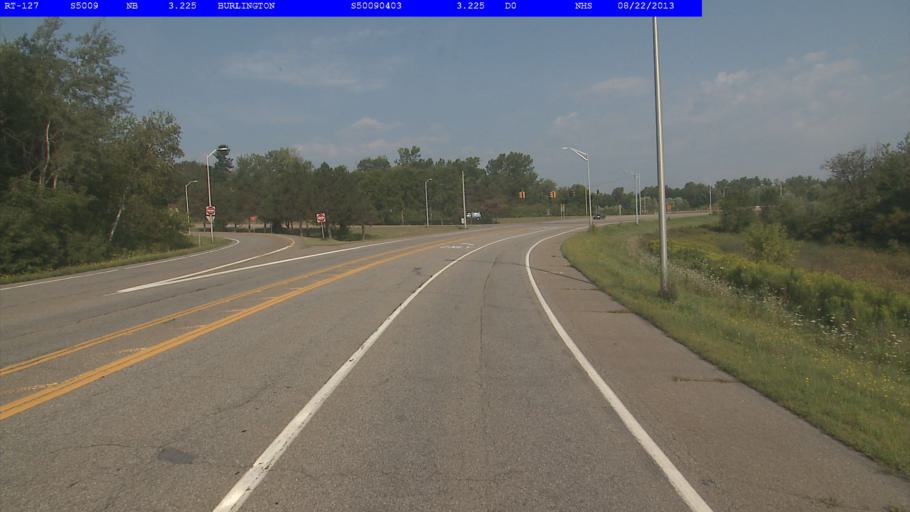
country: US
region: Vermont
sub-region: Chittenden County
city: Burlington
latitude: 44.5221
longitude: -73.2542
